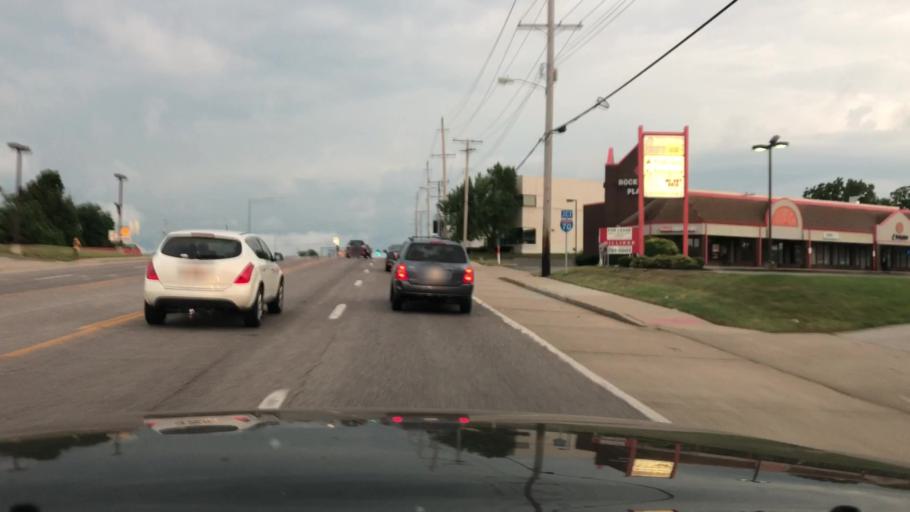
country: US
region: Missouri
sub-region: Saint Louis County
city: Bridgeton
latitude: 38.7453
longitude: -90.4166
